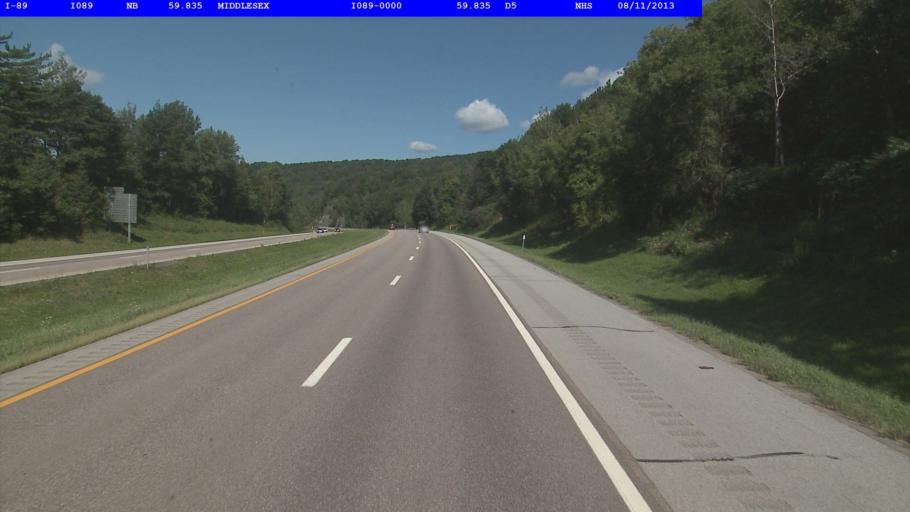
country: US
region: Vermont
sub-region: Washington County
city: Waterbury
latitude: 44.3123
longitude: -72.6954
